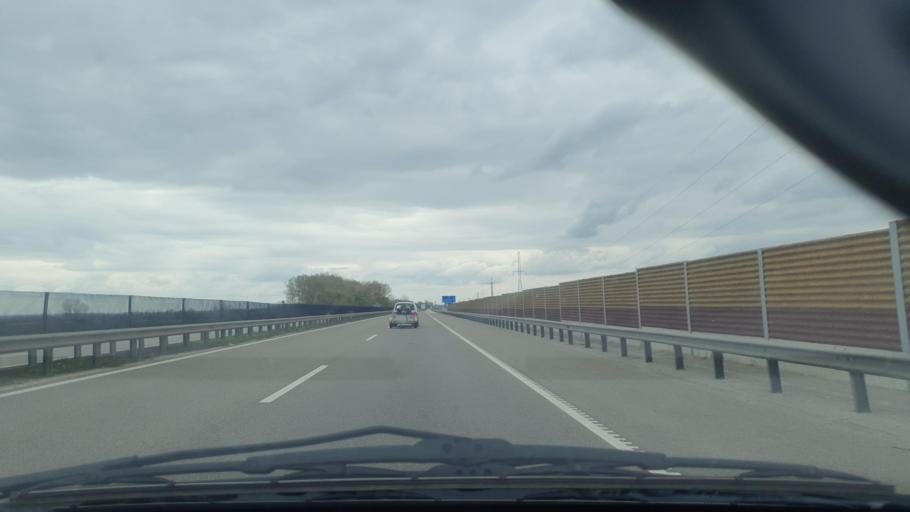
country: HU
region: Pest
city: Cegledbercel
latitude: 47.2120
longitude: 19.7389
